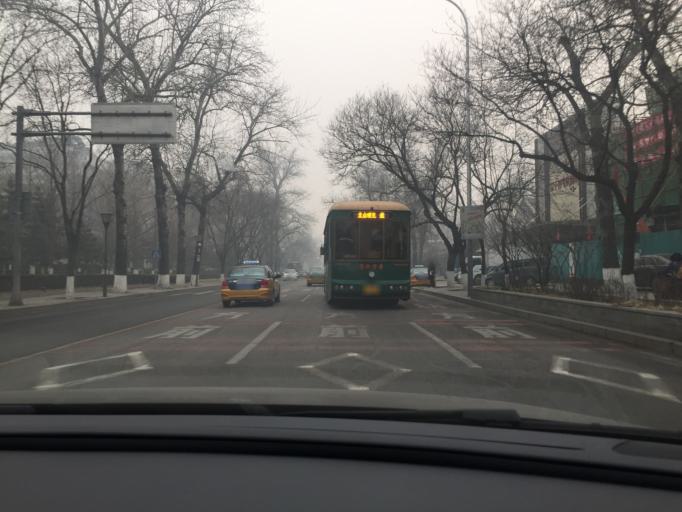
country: CN
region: Beijing
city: Beijing
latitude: 39.9158
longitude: 116.4003
